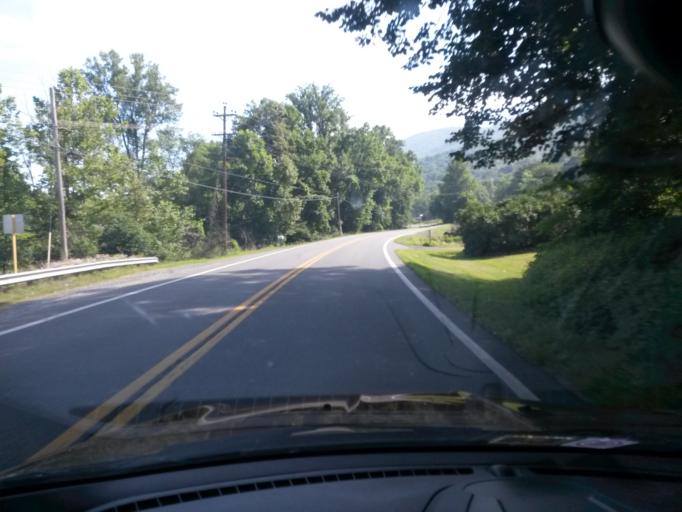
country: US
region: Virginia
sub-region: Rockingham County
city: Broadway
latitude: 38.6817
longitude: -78.9267
